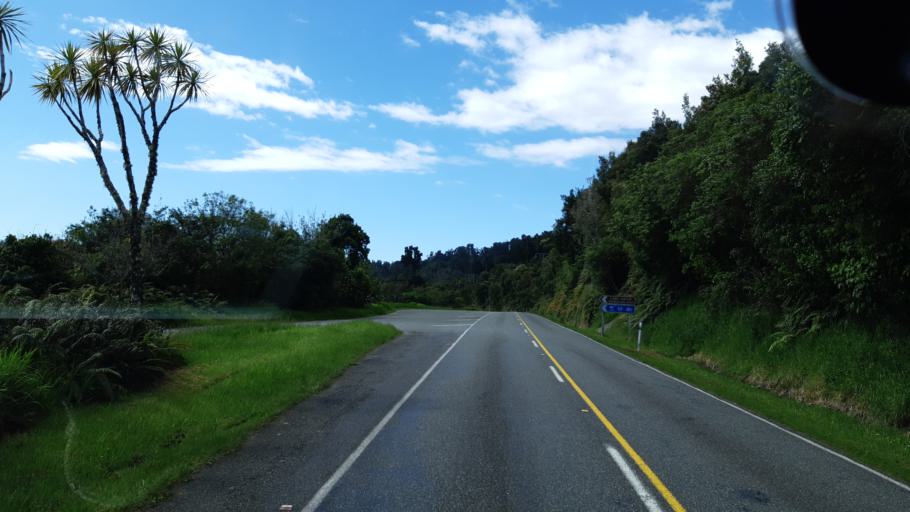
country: NZ
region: West Coast
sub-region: Westland District
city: Hokitika
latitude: -43.0588
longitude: 170.6351
